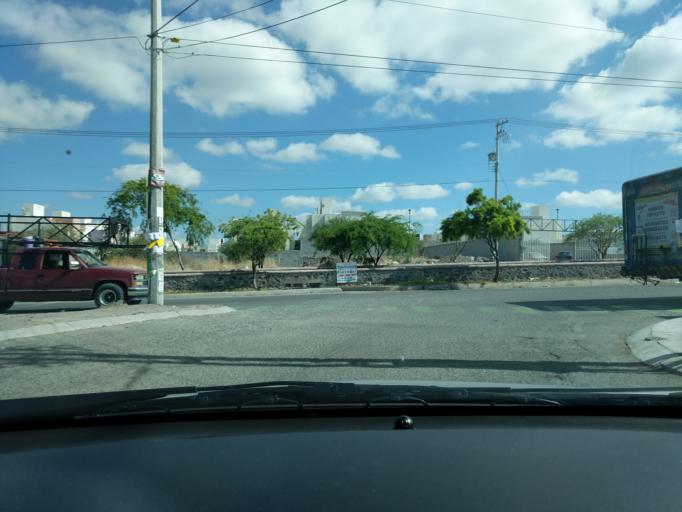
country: MX
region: Queretaro
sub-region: Queretaro
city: Patria Nueva
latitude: 20.6406
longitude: -100.4831
